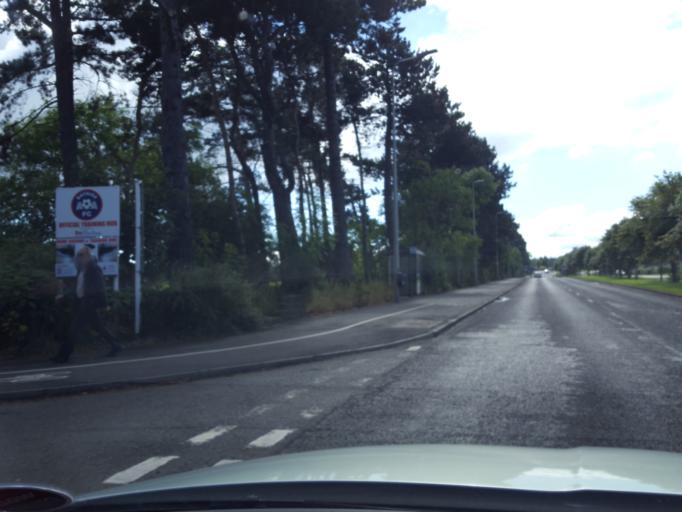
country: GB
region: Scotland
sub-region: Fife
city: Rosyth
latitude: 56.0533
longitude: -3.4349
